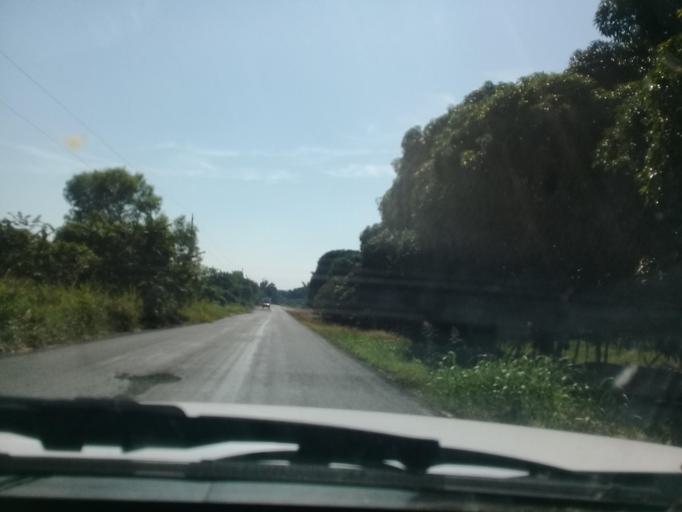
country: MX
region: Veracruz
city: Actopan
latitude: 19.4644
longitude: -96.5746
